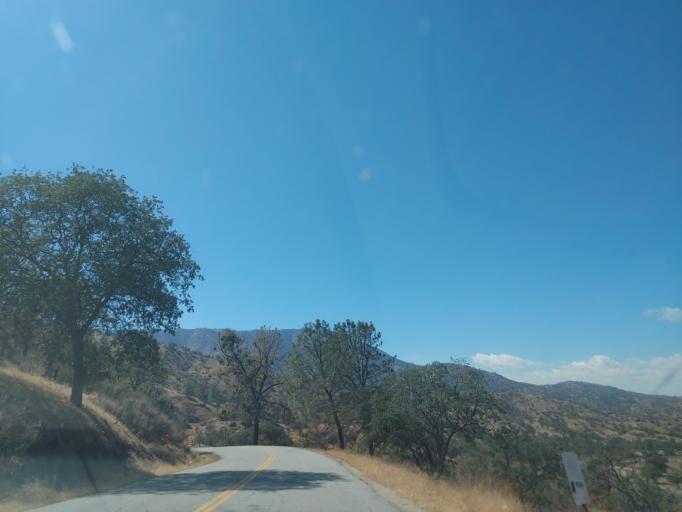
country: US
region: California
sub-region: Kern County
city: Golden Hills
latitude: 35.1952
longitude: -118.5335
